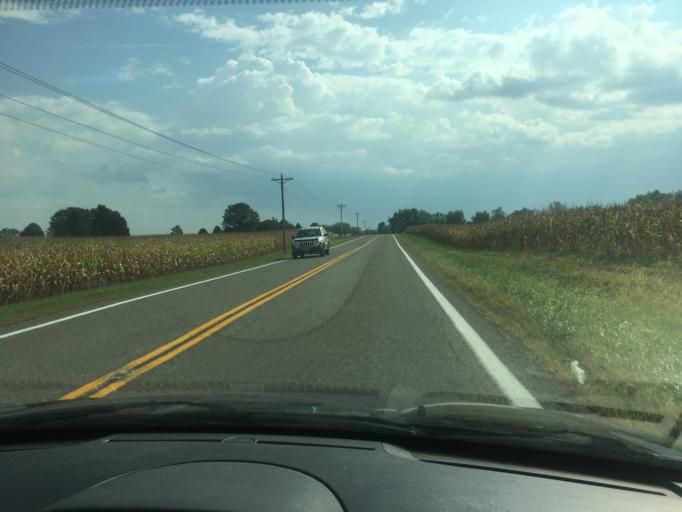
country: US
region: Ohio
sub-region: Champaign County
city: Urbana
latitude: 40.1379
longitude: -83.8350
